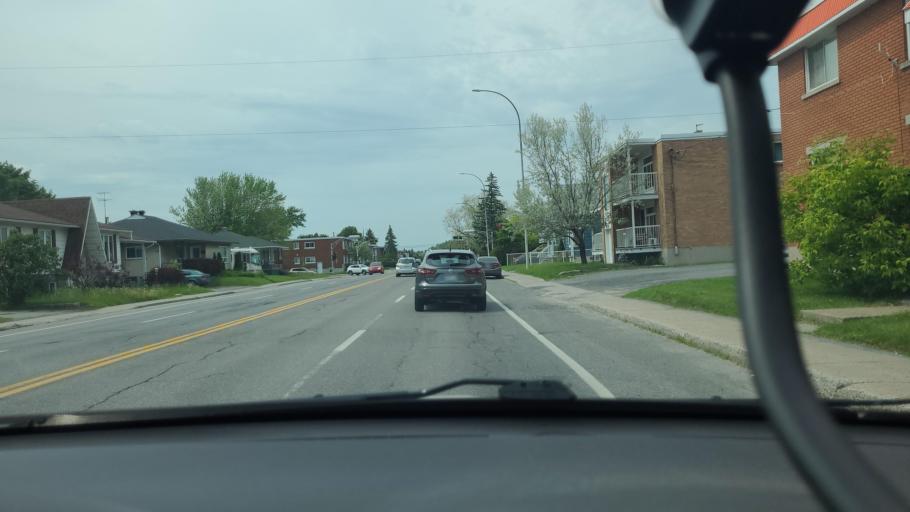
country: CA
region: Quebec
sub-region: Monteregie
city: Saint-Hyacinthe
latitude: 45.6276
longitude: -72.9655
